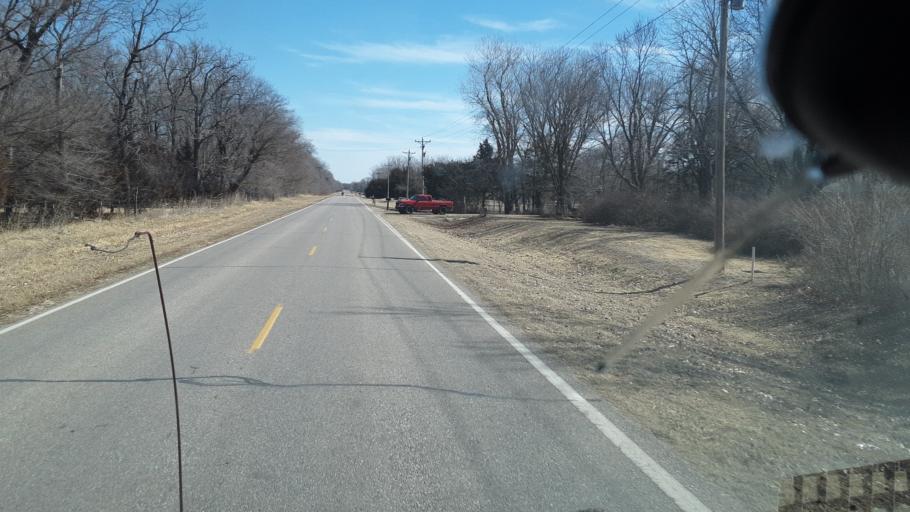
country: US
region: Kansas
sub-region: Reno County
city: Buhler
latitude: 38.1593
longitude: -97.8731
